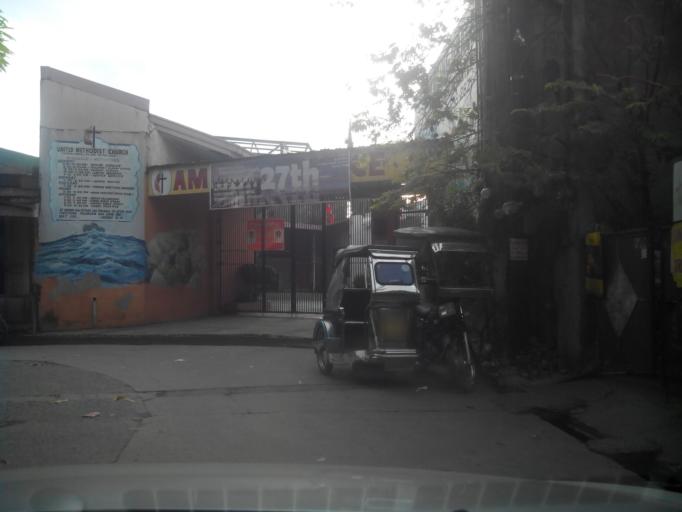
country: PH
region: Calabarzon
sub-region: Province of Rizal
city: Taytay
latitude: 14.5648
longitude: 121.1246
